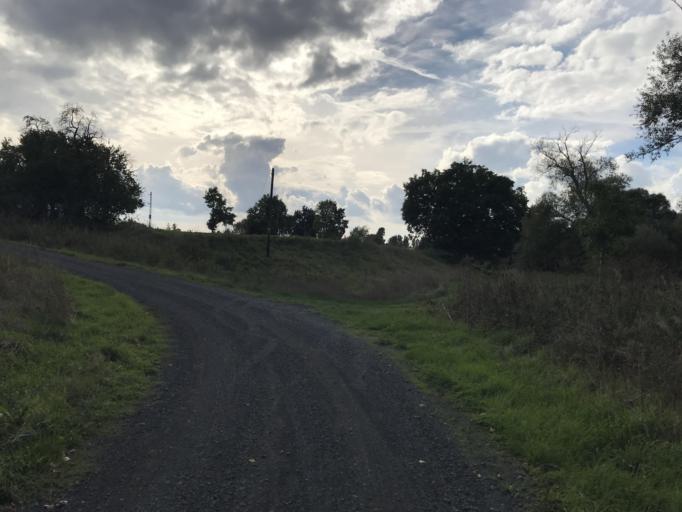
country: DE
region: Hesse
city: Felsberg
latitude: 51.1190
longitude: 9.4121
